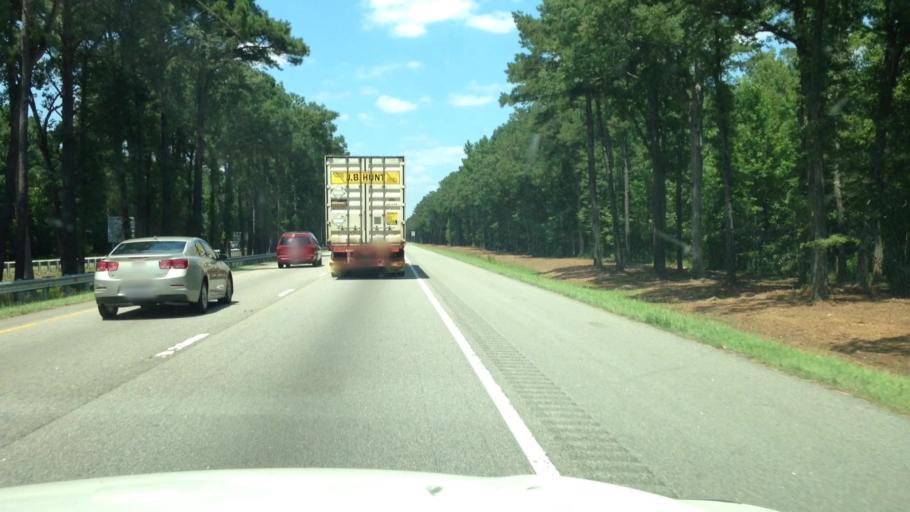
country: US
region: North Carolina
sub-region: Robeson County
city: Lumberton
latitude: 34.6809
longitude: -79.0022
